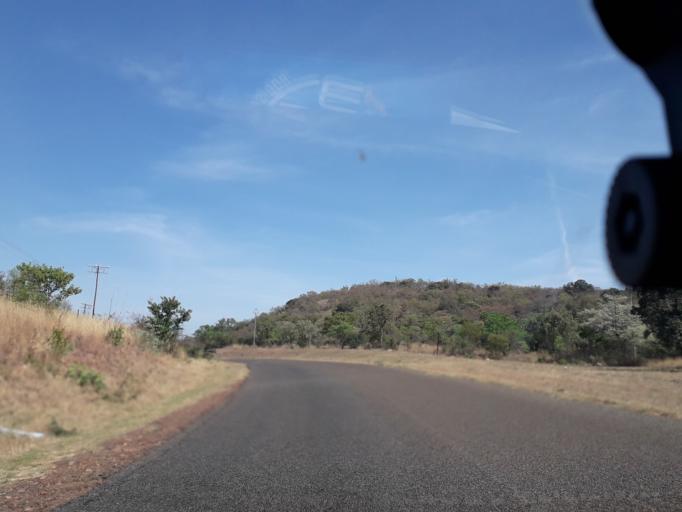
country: ZA
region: Limpopo
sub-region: Waterberg District Municipality
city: Warmbaths
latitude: -24.8426
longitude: 28.2502
